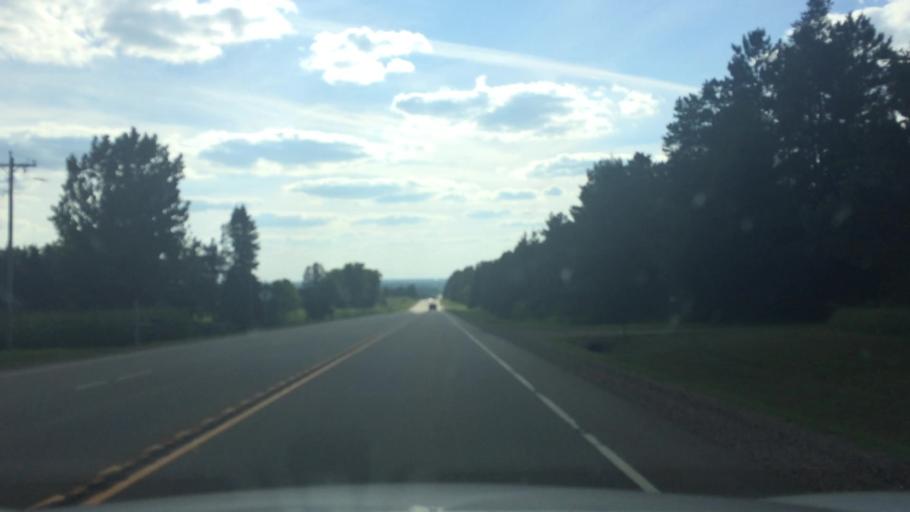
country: US
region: Wisconsin
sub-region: Lincoln County
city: Merrill
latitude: 45.1780
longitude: -89.6158
